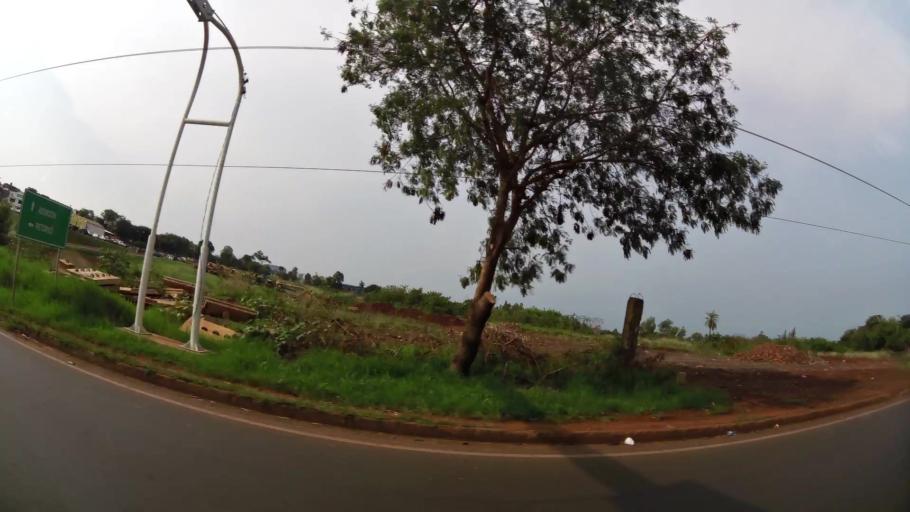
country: PY
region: Alto Parana
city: Ciudad del Este
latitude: -25.5032
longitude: -54.6497
